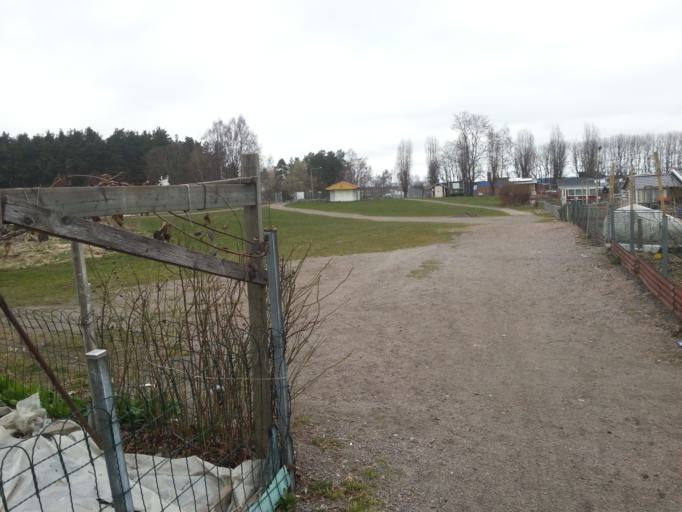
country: SE
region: OEstergoetland
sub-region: Norrkopings Kommun
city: Norrkoping
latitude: 58.5927
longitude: 16.1536
